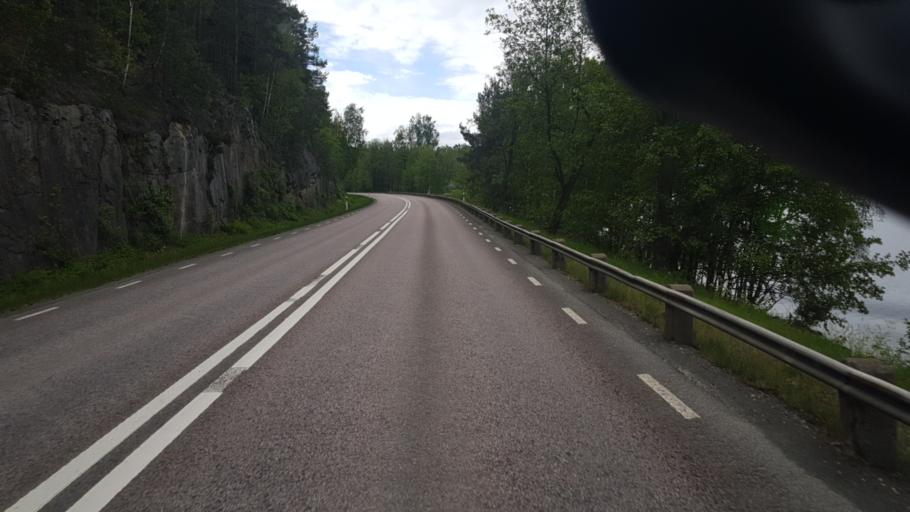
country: SE
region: Vaermland
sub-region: Eda Kommun
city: Amotfors
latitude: 59.7447
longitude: 12.4860
